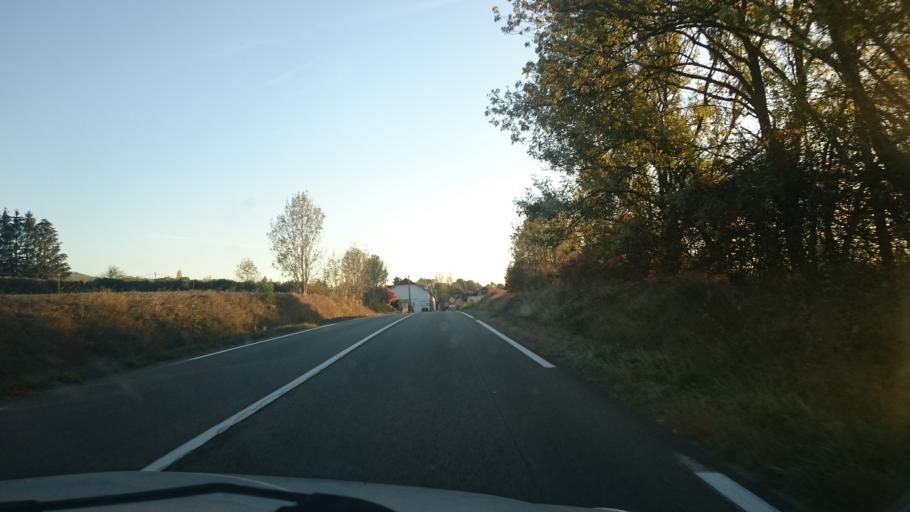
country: FR
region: Franche-Comte
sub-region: Departement du Doubs
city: Quingey
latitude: 47.0557
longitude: 5.8806
